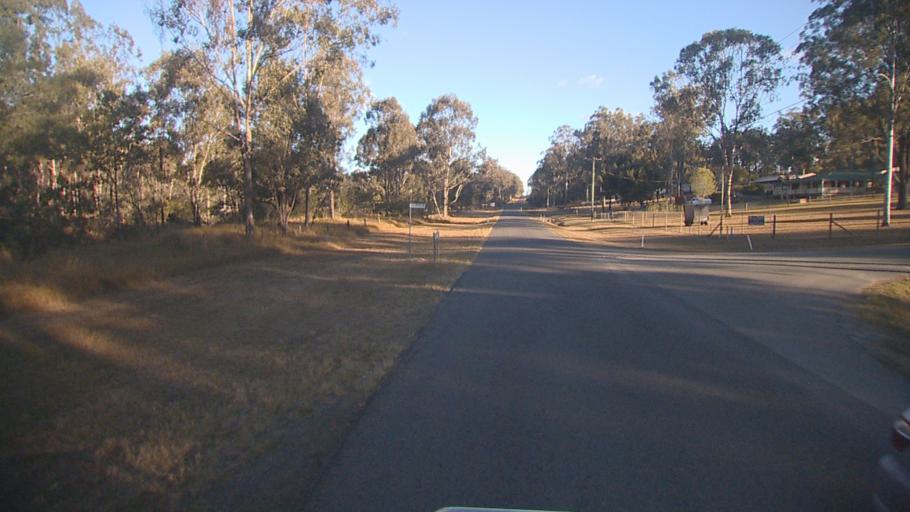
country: AU
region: Queensland
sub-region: Logan
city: Cedar Vale
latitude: -27.8633
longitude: 152.9775
